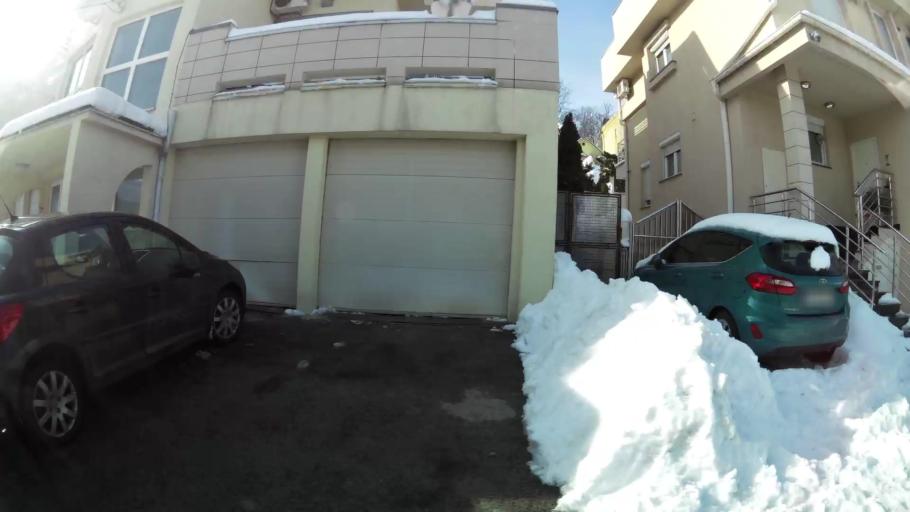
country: RS
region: Central Serbia
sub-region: Belgrade
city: Palilula
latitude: 44.7949
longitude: 20.5191
